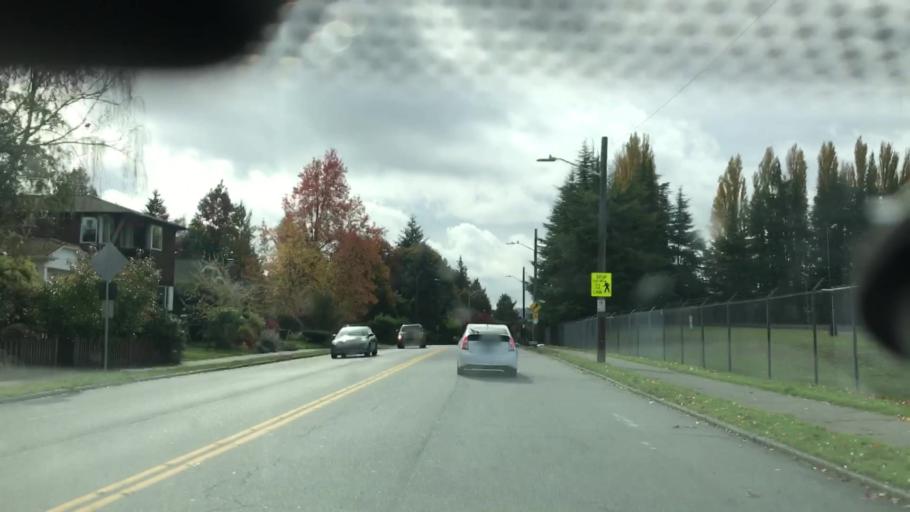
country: US
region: Washington
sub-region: King County
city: Seattle
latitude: 47.6820
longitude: -122.3117
